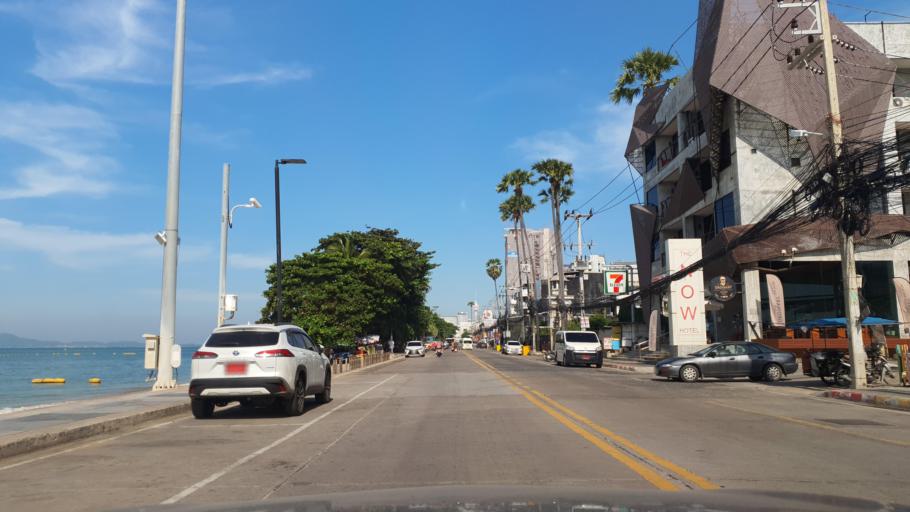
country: TH
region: Chon Buri
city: Phatthaya
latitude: 12.8827
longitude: 100.8809
